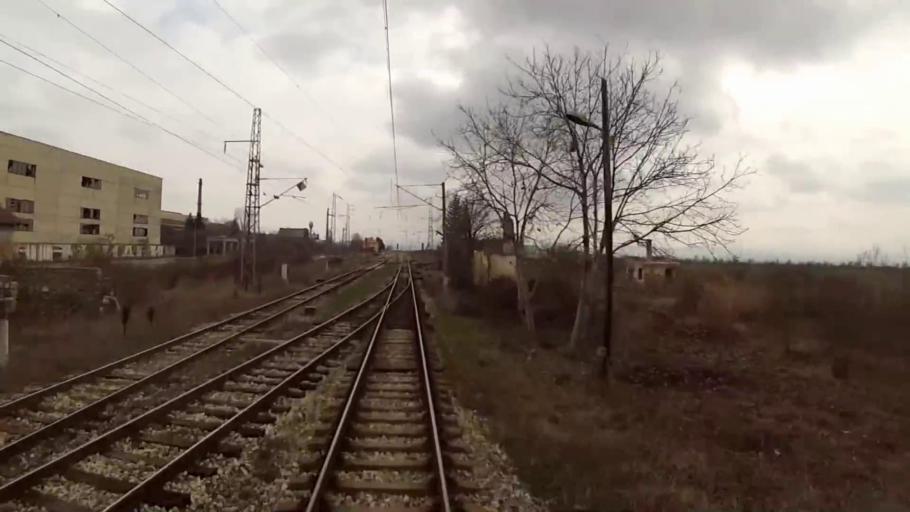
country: BG
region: Sofiya
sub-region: Obshtina Gorna Malina
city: Gorna Malina
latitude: 42.7013
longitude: 23.6475
